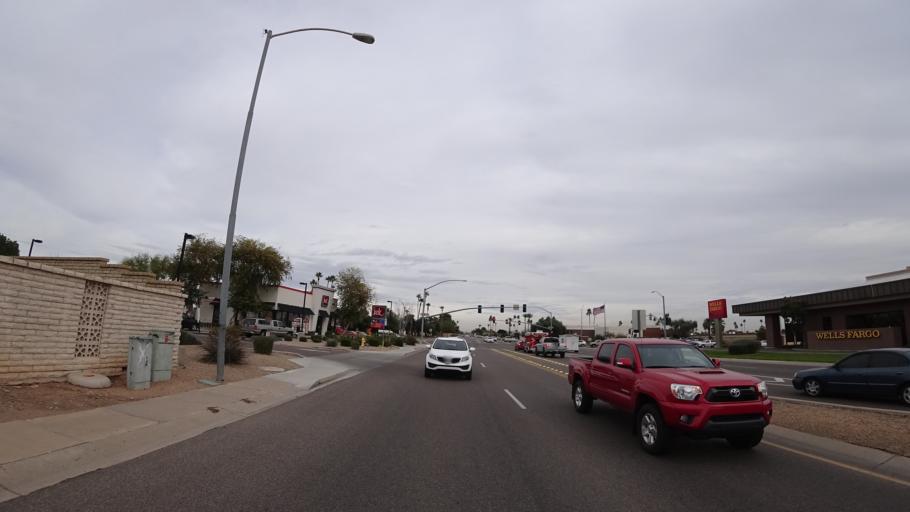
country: US
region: Arizona
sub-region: Maricopa County
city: Sun City
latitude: 33.6094
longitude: -112.2687
